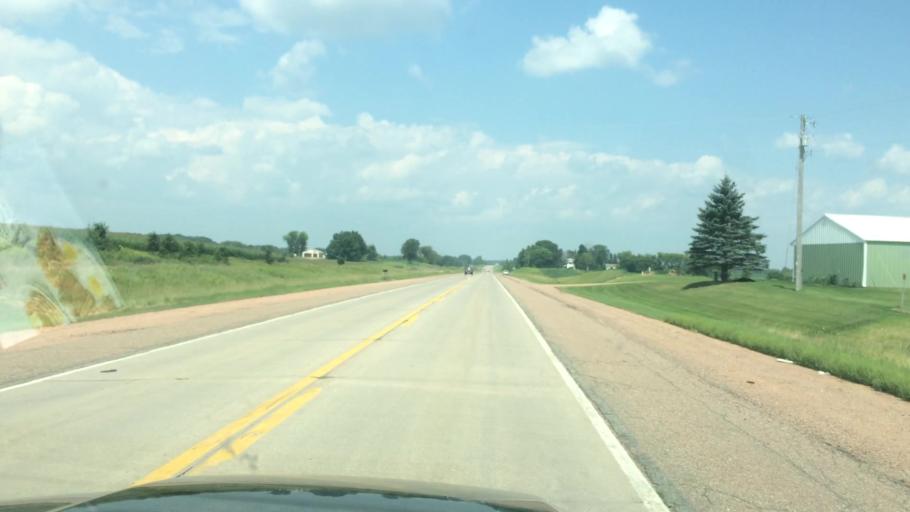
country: US
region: Wisconsin
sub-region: Clark County
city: Colby
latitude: 44.8645
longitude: -90.3158
